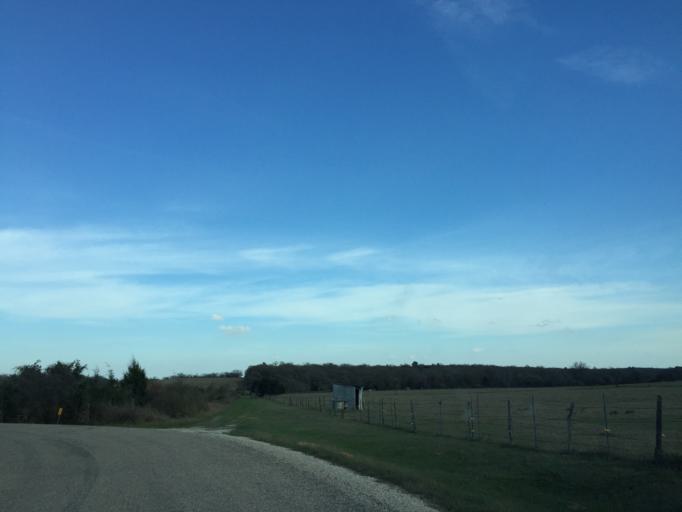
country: US
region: Texas
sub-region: Milam County
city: Thorndale
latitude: 30.4470
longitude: -97.1960
